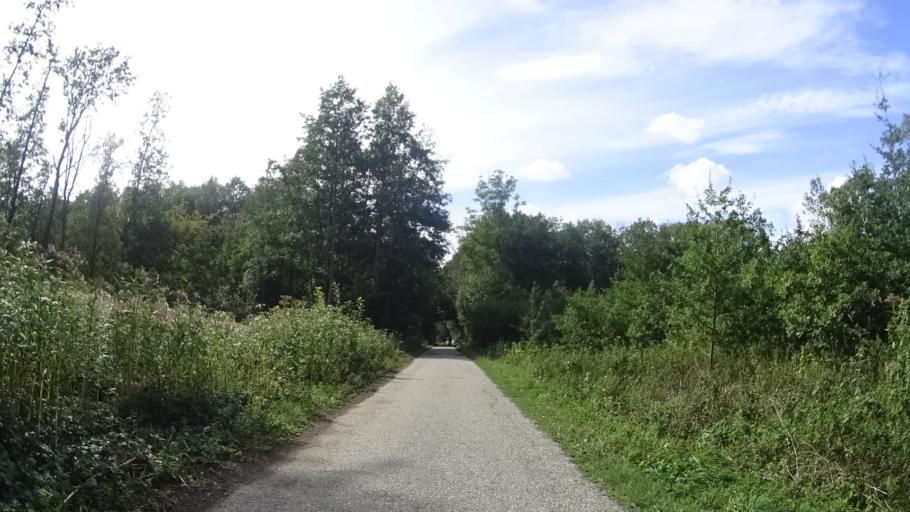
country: CZ
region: Olomoucky
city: Naklo
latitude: 49.6823
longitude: 17.1437
